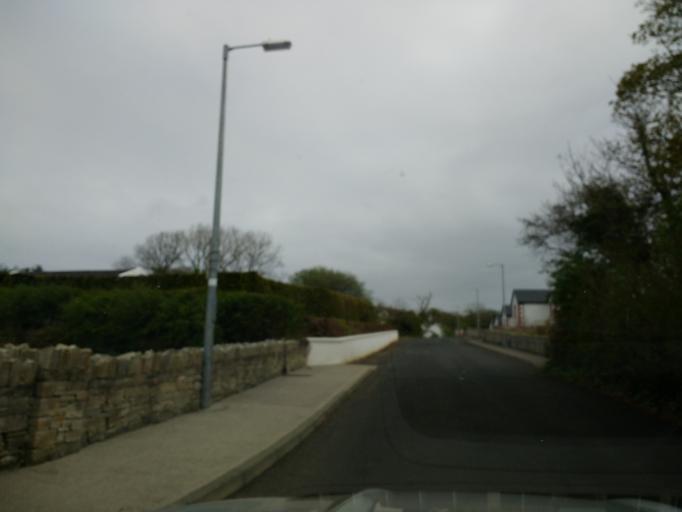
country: IE
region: Ulster
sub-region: County Donegal
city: Ramelton
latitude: 55.2084
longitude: -7.6222
